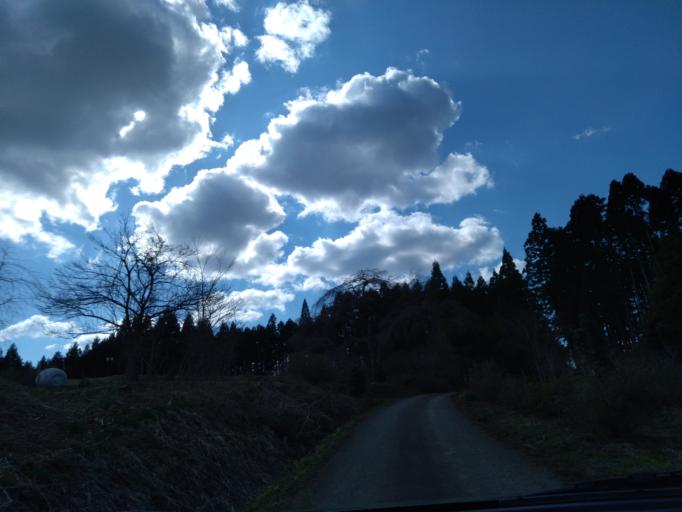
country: JP
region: Iwate
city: Ichinoseki
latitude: 38.9802
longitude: 141.0168
